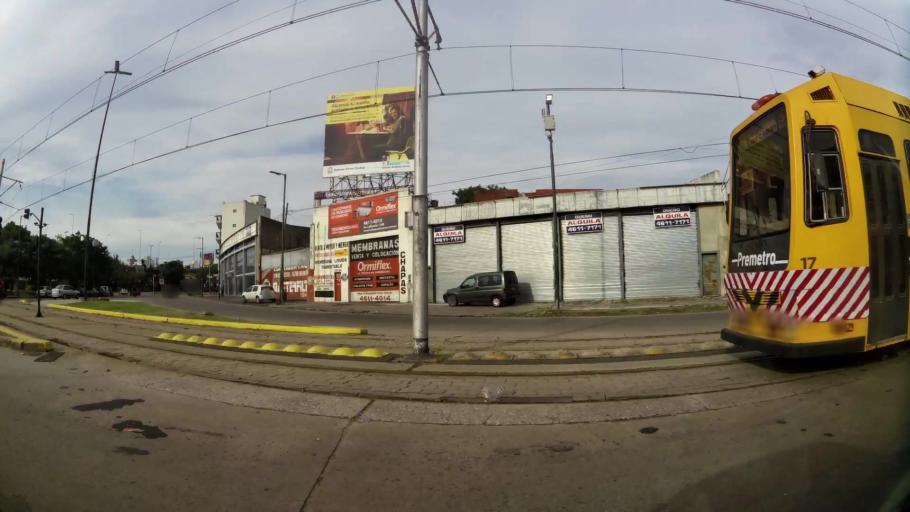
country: AR
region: Buenos Aires F.D.
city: Villa Lugano
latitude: -34.6443
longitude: -58.4609
